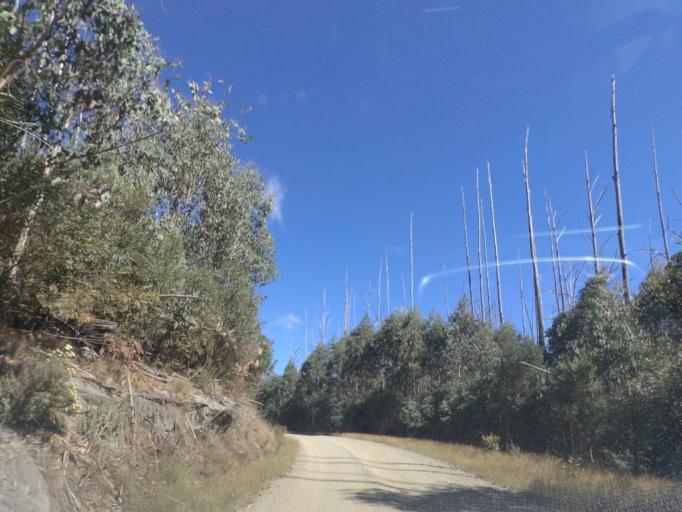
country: AU
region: Victoria
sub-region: Murrindindi
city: Alexandra
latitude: -37.4173
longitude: 145.8000
